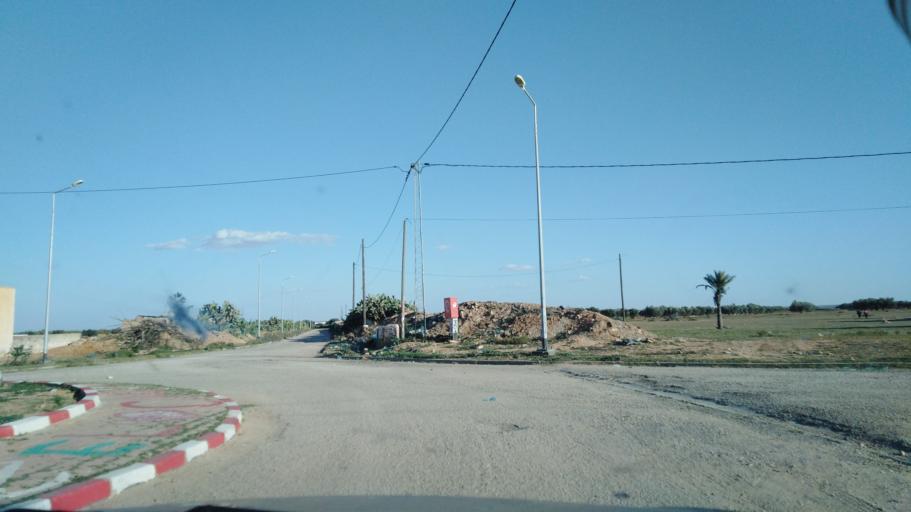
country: TN
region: Al Mahdiyah
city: Shurban
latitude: 34.9606
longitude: 10.3659
